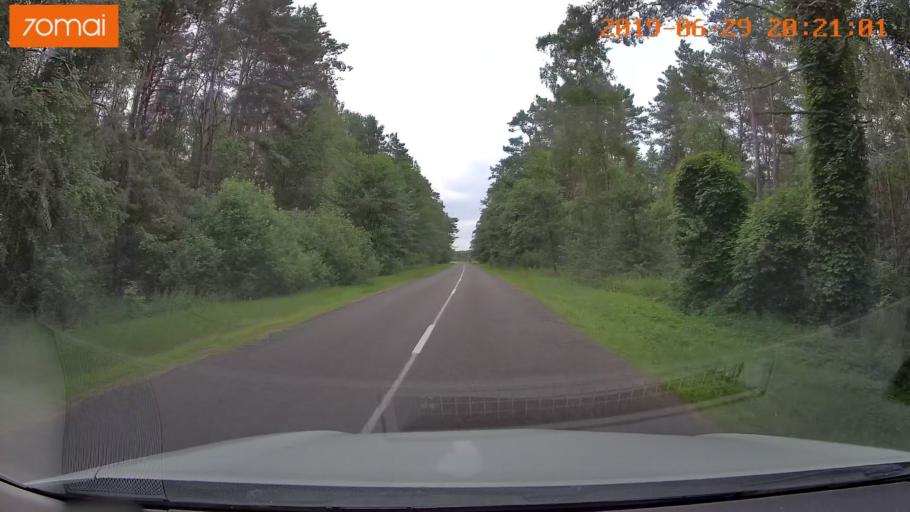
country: BY
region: Brest
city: Asnyezhytsy
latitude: 52.4155
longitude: 26.2516
